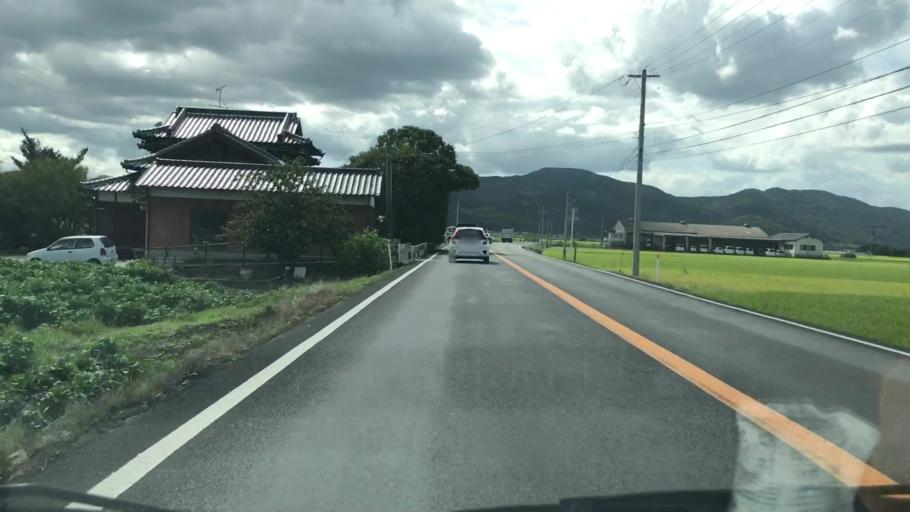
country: JP
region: Saga Prefecture
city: Kashima
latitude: 33.1397
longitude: 130.1341
